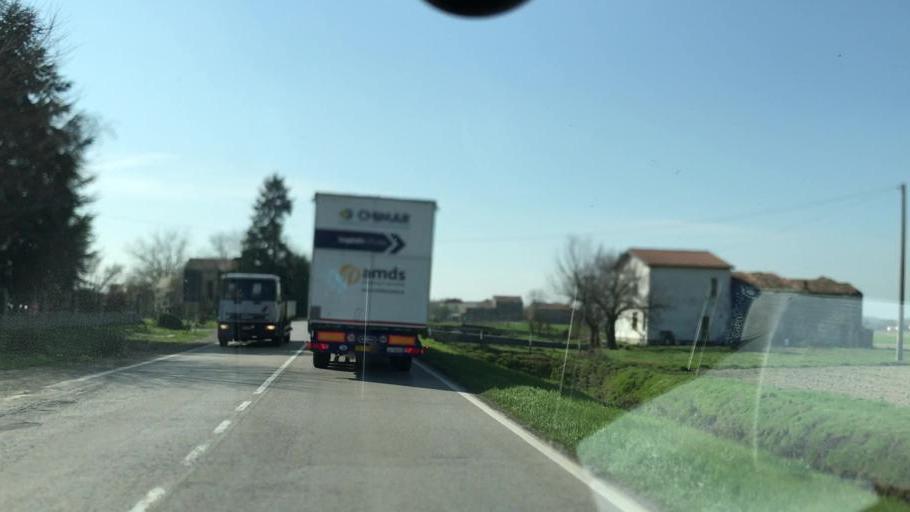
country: IT
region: Veneto
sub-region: Provincia di Rovigo
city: Castelnovo Bariano
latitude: 45.0330
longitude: 11.2987
